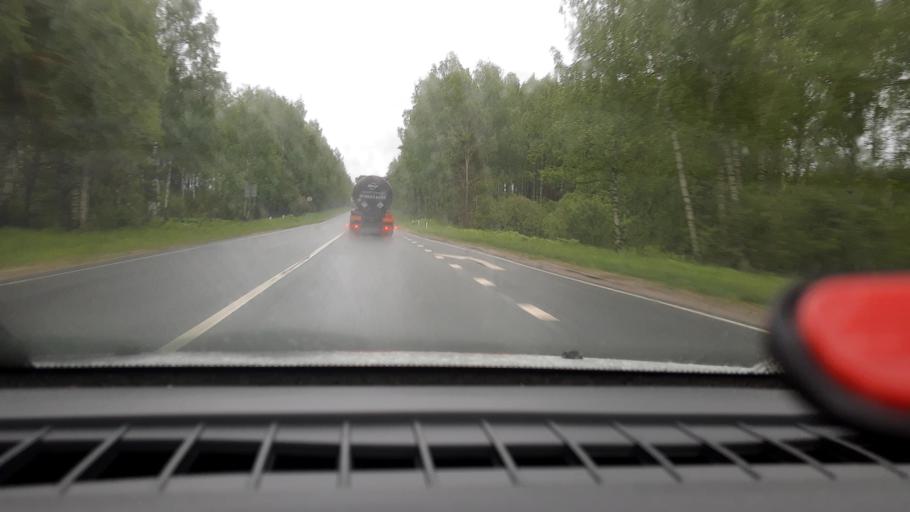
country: RU
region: Nizjnij Novgorod
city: Sukhobezvodnoye
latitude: 56.8605
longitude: 44.8855
